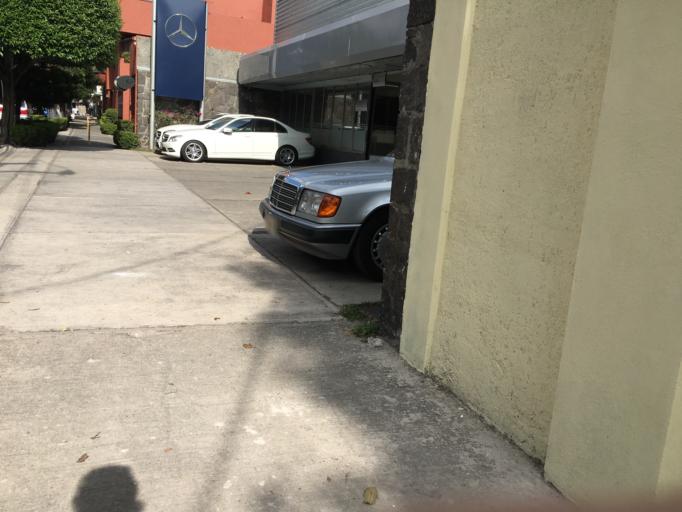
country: MX
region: Mexico City
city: Colonia del Valle
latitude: 19.3761
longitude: -99.1685
